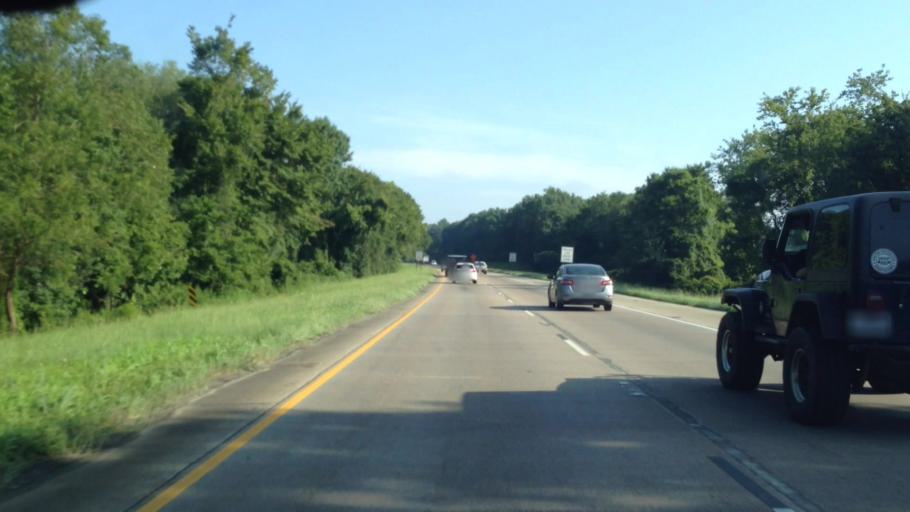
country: US
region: Louisiana
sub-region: Ascension Parish
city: Prairieville
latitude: 30.3050
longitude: -90.9933
